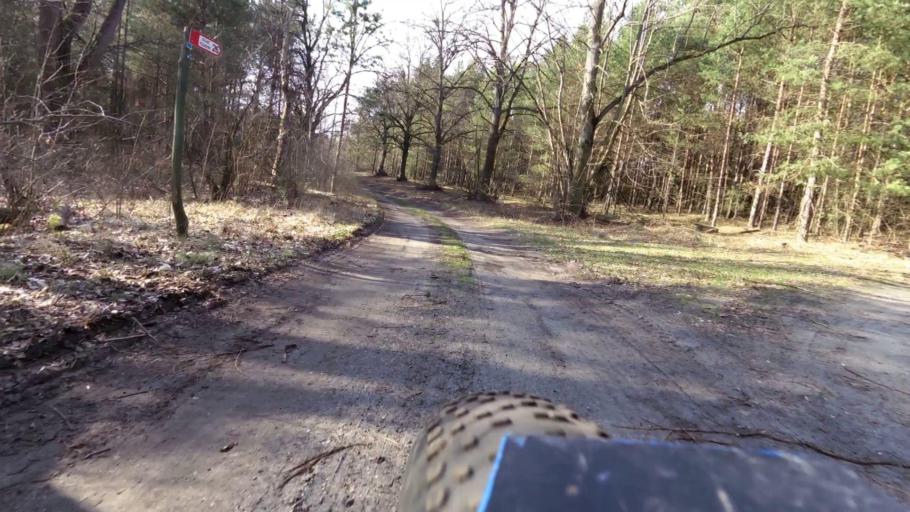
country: PL
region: Lubusz
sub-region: Powiat slubicki
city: Cybinka
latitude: 52.2397
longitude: 14.7827
